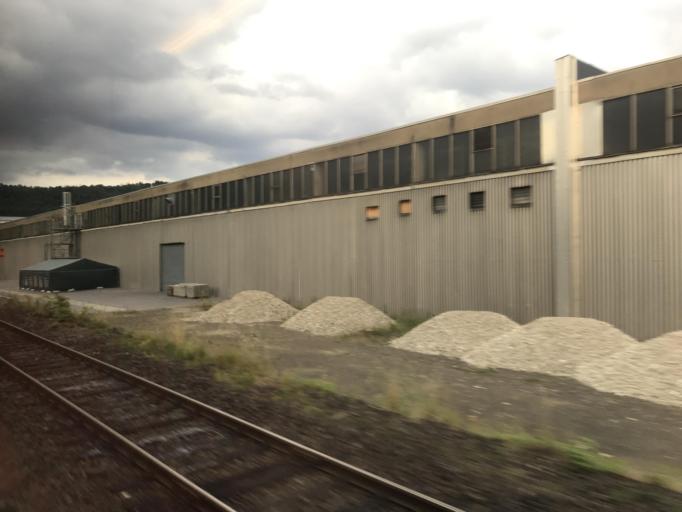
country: DE
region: Rheinland-Pfalz
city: Wallmenroth
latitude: 50.7958
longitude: 7.8455
